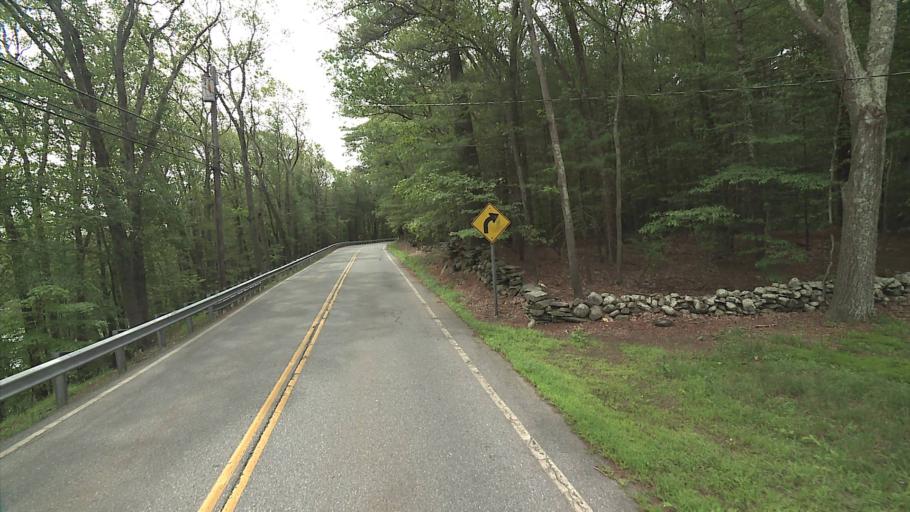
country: US
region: Massachusetts
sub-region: Worcester County
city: Webster
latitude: 42.0129
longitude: -71.8445
